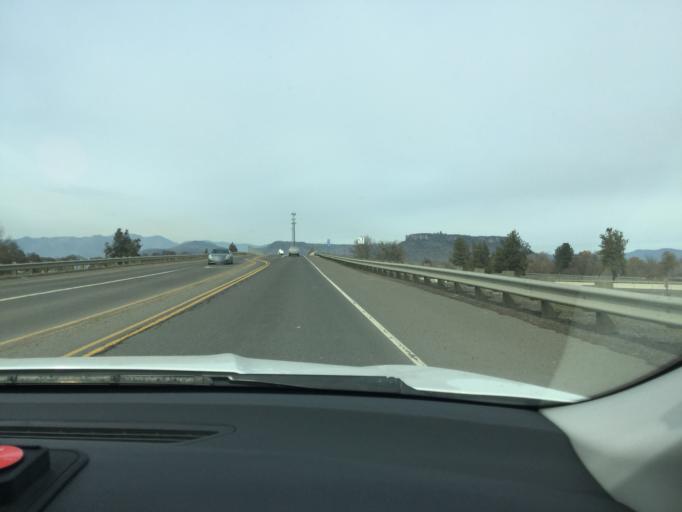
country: US
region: Oregon
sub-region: Jackson County
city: Central Point
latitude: 42.4038
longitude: -122.9413
